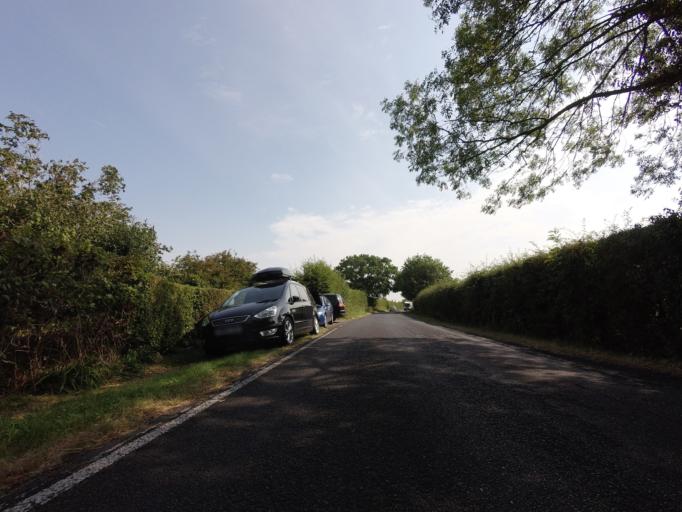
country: GB
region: England
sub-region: Kent
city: Staplehurst
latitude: 51.1365
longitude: 0.5848
